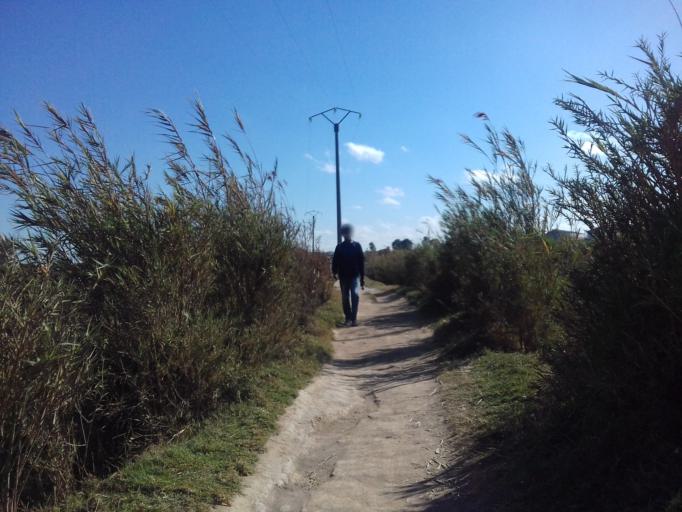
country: MG
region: Analamanga
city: Antananarivo
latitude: -18.8901
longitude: 47.4855
